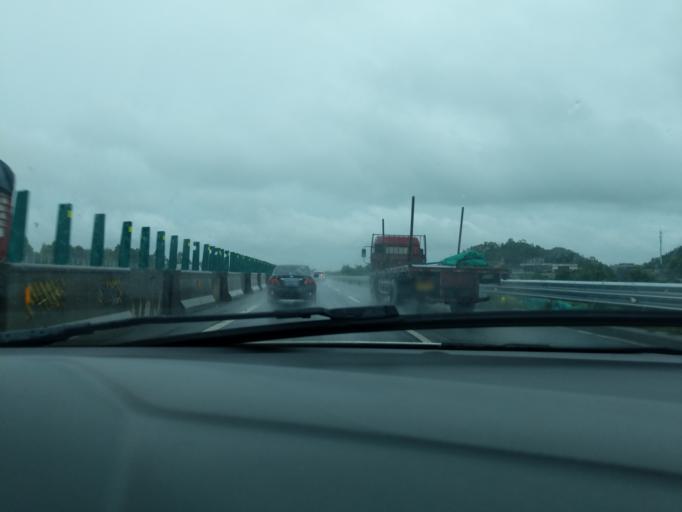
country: CN
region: Guangdong
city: Yueshan
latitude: 22.4629
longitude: 112.7223
